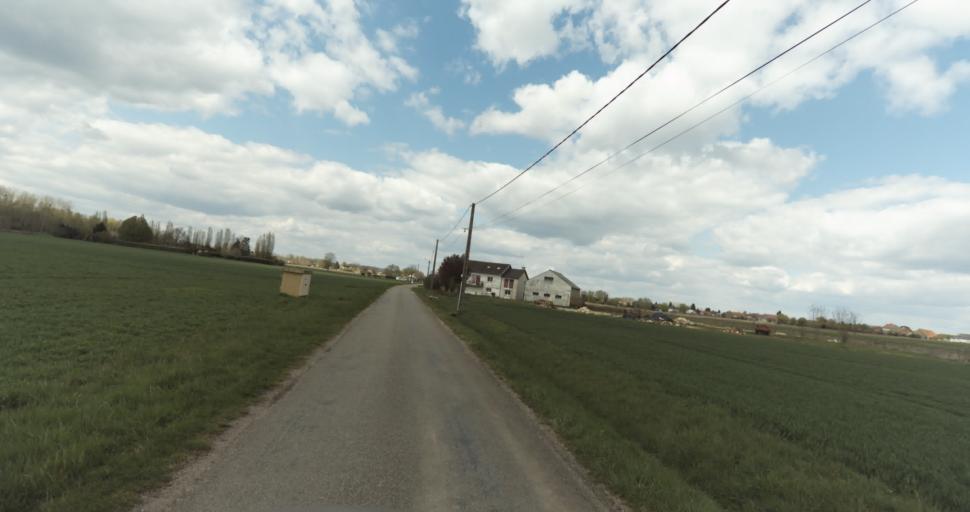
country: FR
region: Bourgogne
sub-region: Departement de la Cote-d'Or
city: Auxonne
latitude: 47.1763
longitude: 5.3942
